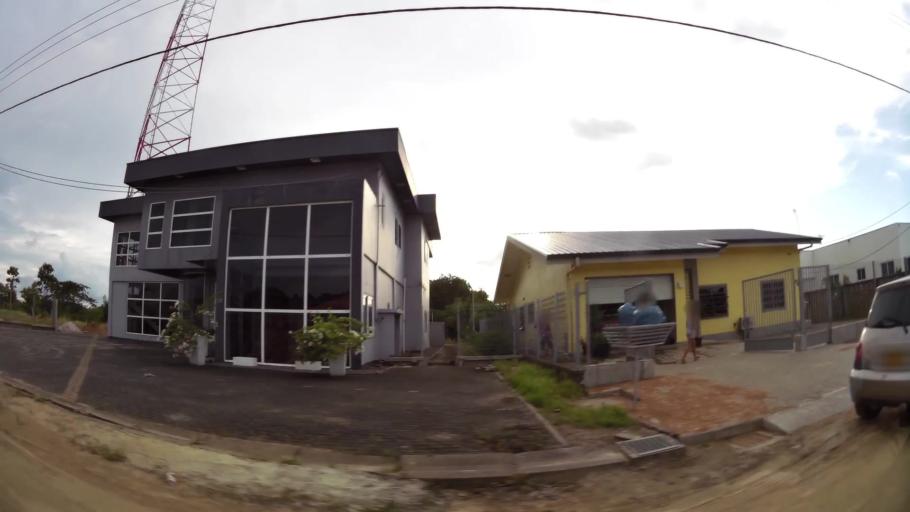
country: SR
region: Paramaribo
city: Paramaribo
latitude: 5.8616
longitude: -55.1804
